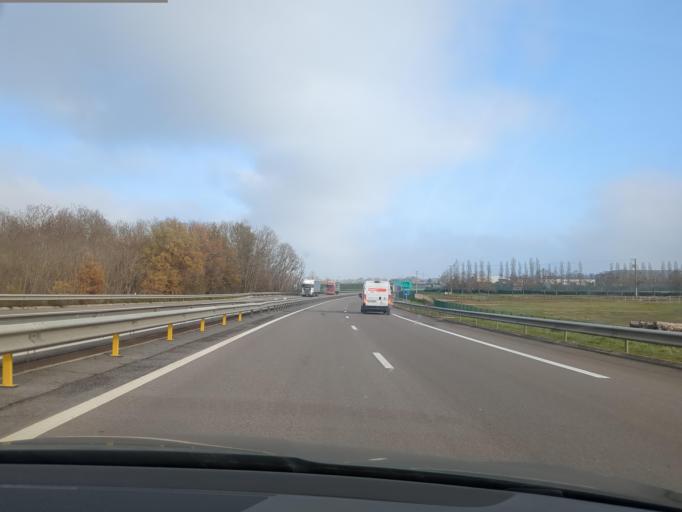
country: FR
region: Bourgogne
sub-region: Departement de Saone-et-Loire
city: Paray-le-Monial
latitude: 46.4679
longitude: 4.0918
